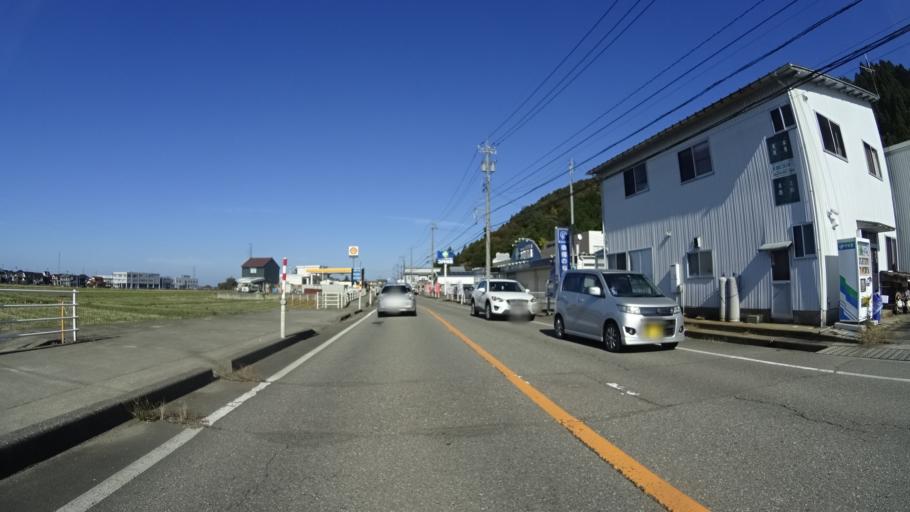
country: JP
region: Ishikawa
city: Tsurugi-asahimachi
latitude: 36.4656
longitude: 136.6194
